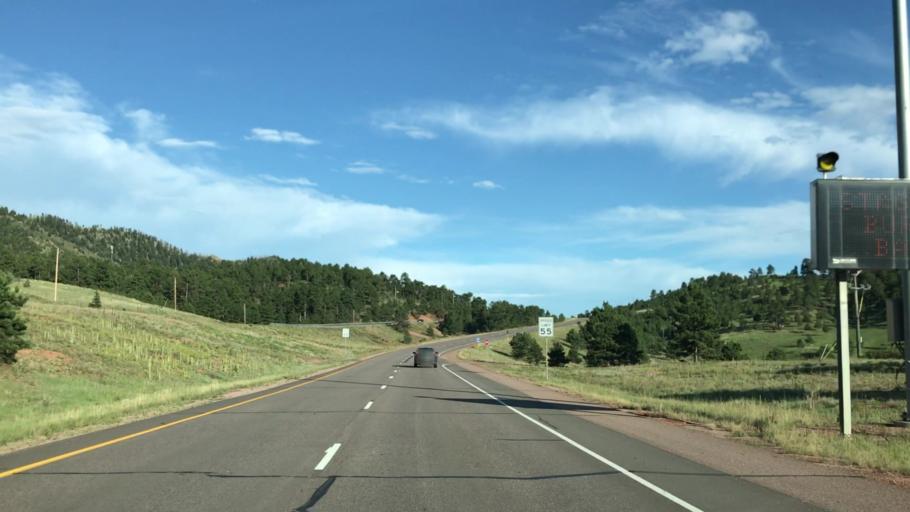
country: US
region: Colorado
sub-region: El Paso County
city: Cascade-Chipita Park
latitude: 38.9402
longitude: -105.0139
